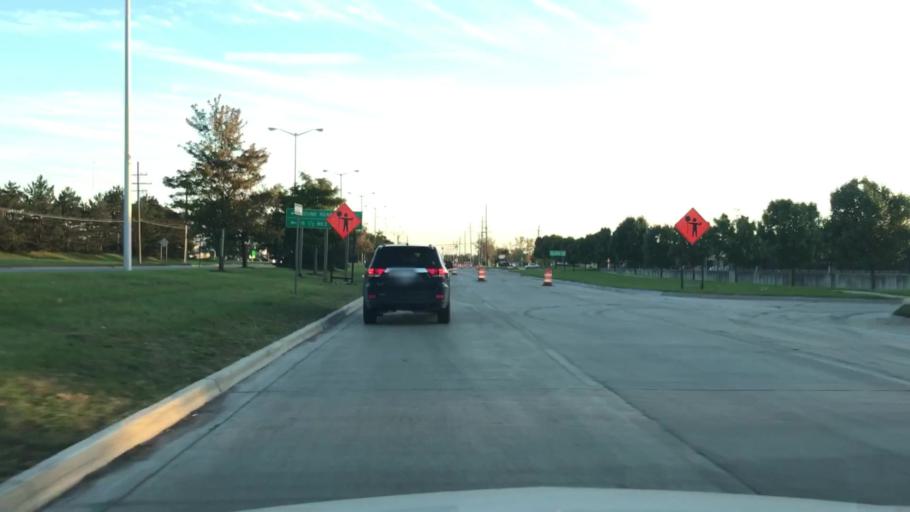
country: US
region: Michigan
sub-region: Macomb County
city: Sterling Heights
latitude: 42.5970
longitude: -83.0509
